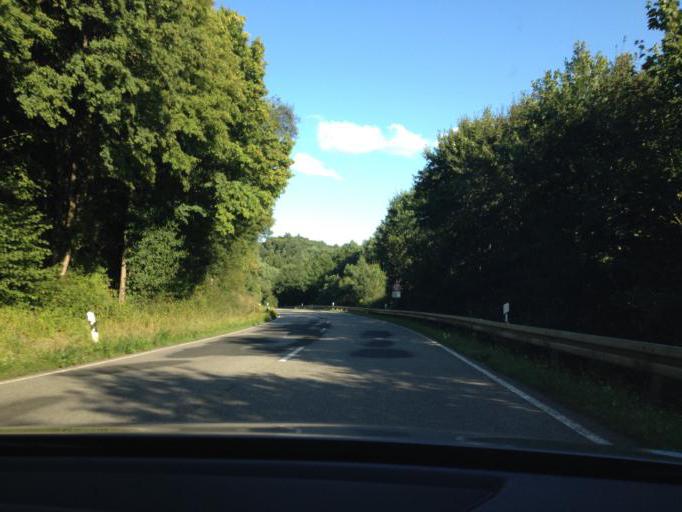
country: DE
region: Saarland
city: Schmelz
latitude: 49.4827
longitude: 6.8710
